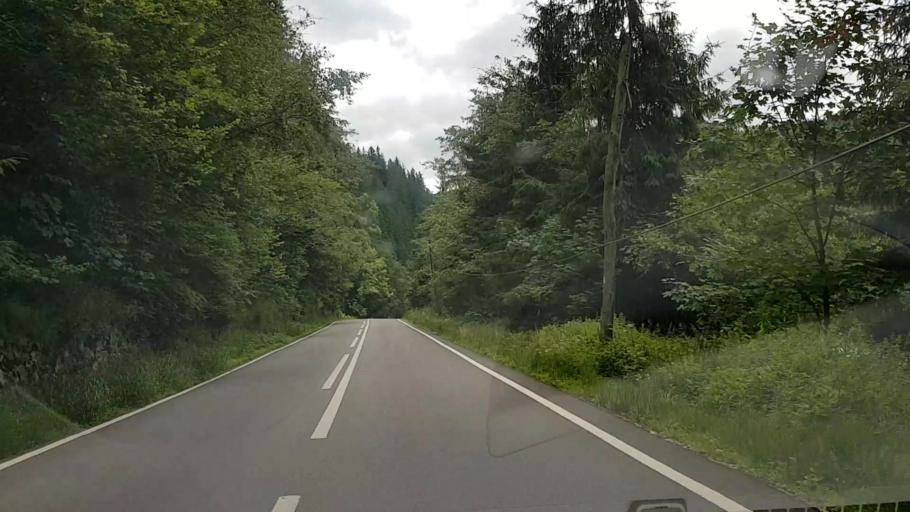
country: RO
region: Suceava
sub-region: Comuna Crucea
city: Crucea
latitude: 47.3667
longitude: 25.5908
